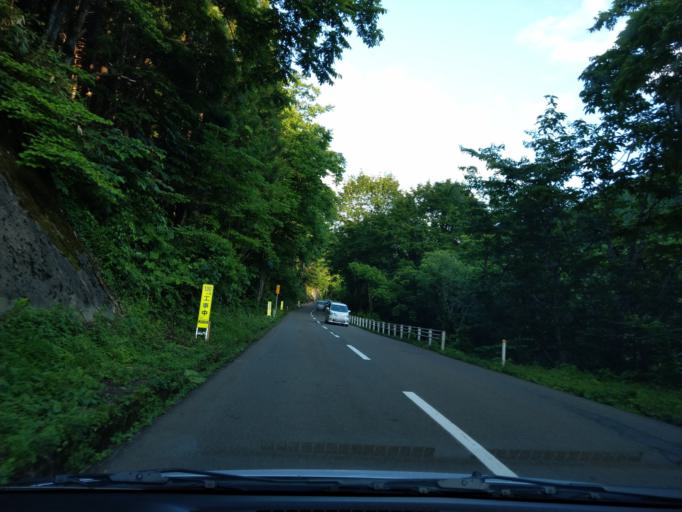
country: JP
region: Akita
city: Kakunodatemachi
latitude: 39.8829
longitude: 140.4715
